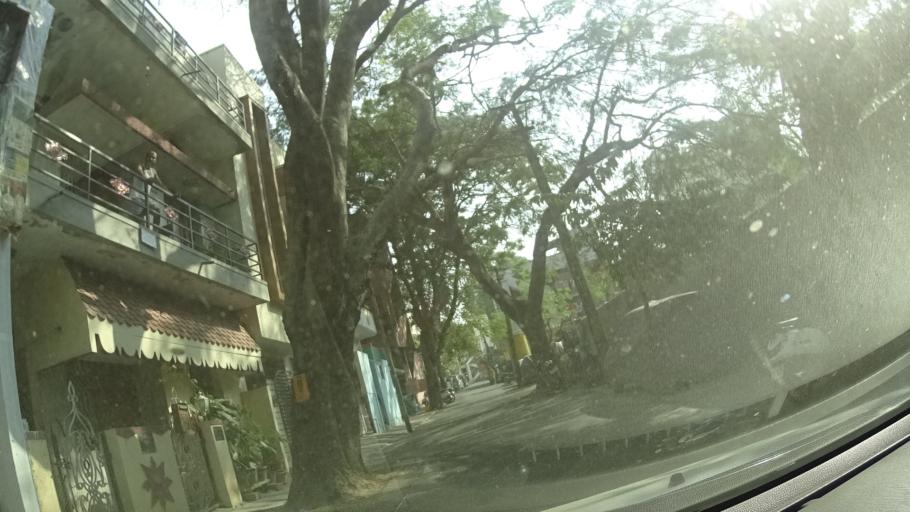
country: IN
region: Karnataka
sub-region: Bangalore Urban
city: Bangalore
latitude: 12.9480
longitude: 77.5595
